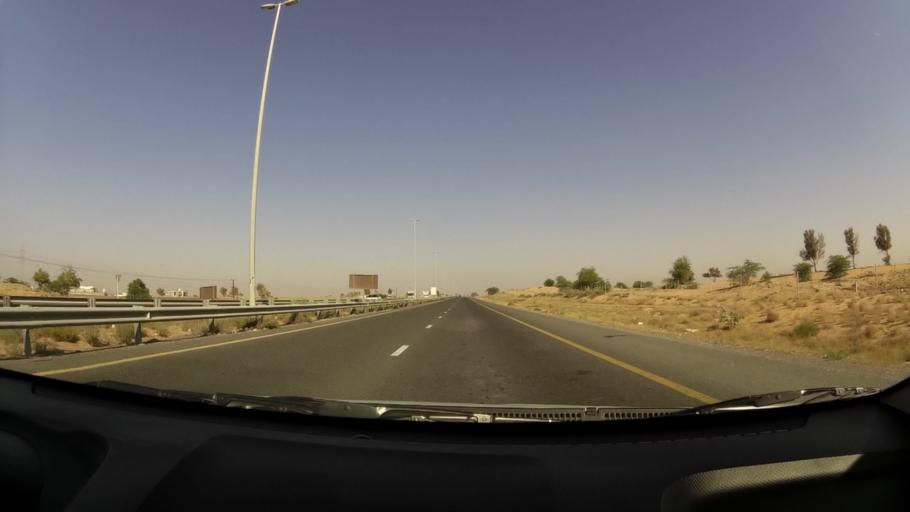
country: AE
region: Umm al Qaywayn
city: Umm al Qaywayn
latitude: 25.4650
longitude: 55.5956
